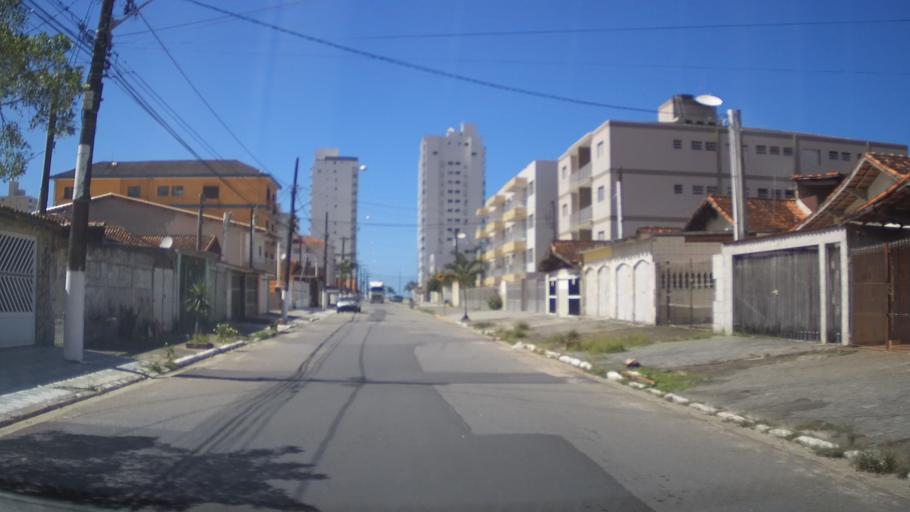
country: BR
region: Sao Paulo
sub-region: Praia Grande
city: Praia Grande
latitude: -24.0432
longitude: -46.5137
